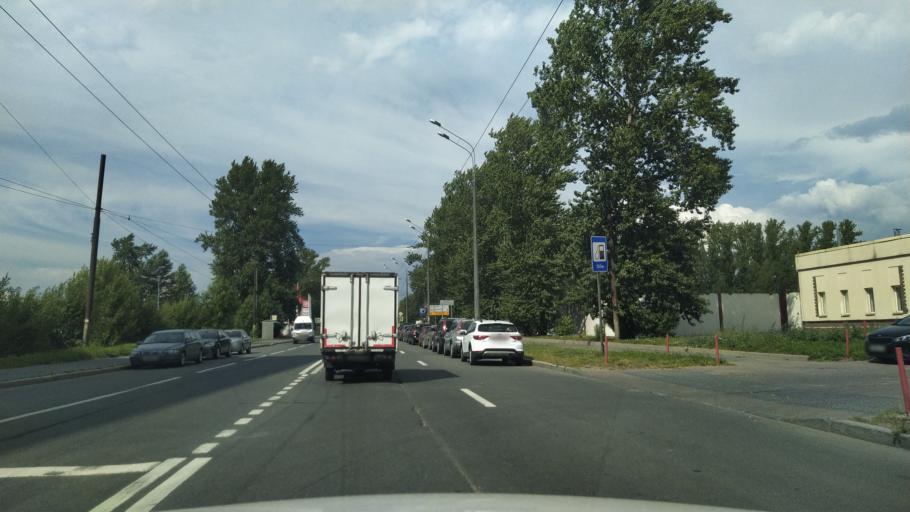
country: RU
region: Leningrad
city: Finlyandskiy
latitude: 59.9636
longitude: 30.3682
